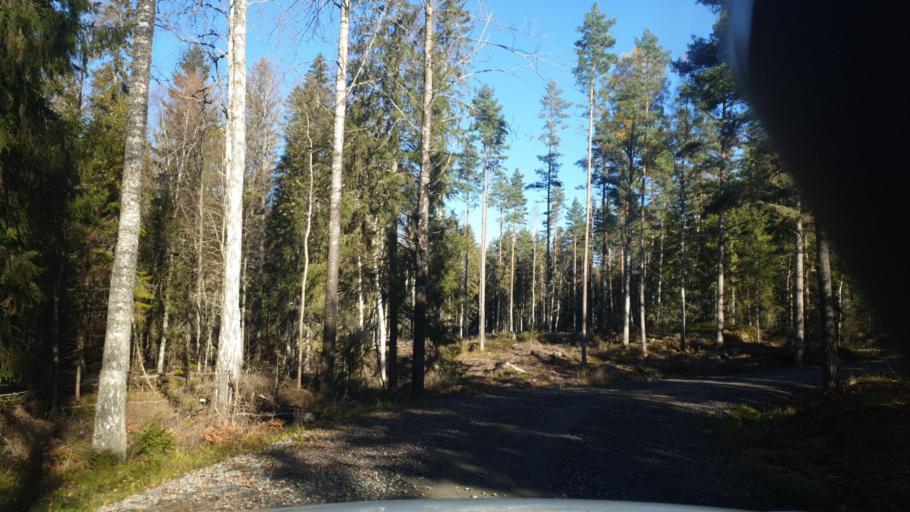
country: SE
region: Vaermland
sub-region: Karlstads Kommun
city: Valberg
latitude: 59.4533
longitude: 13.0942
